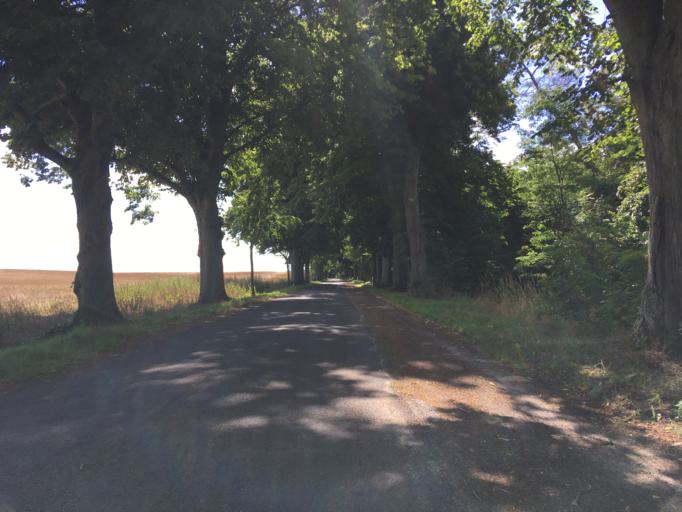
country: DE
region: Brandenburg
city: Templin
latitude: 53.1789
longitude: 13.5375
